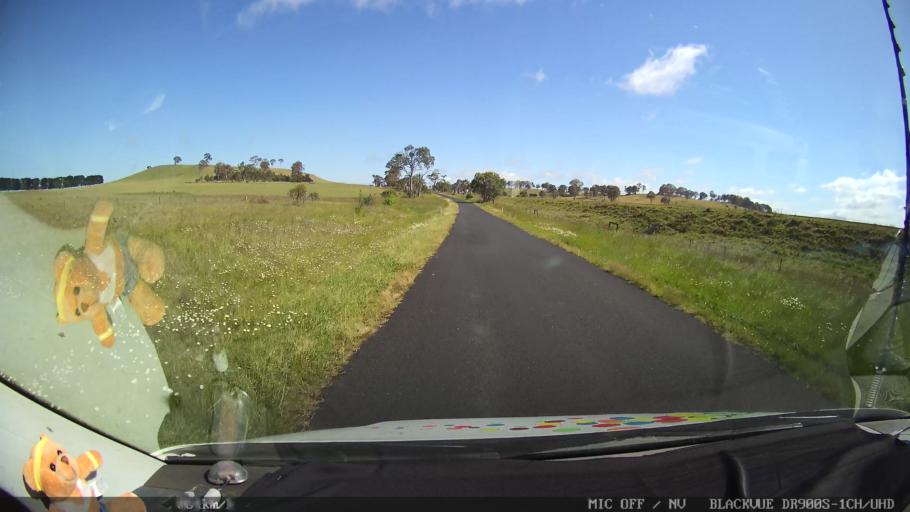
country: AU
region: New South Wales
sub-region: Guyra
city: Guyra
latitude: -30.1694
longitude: 151.6850
